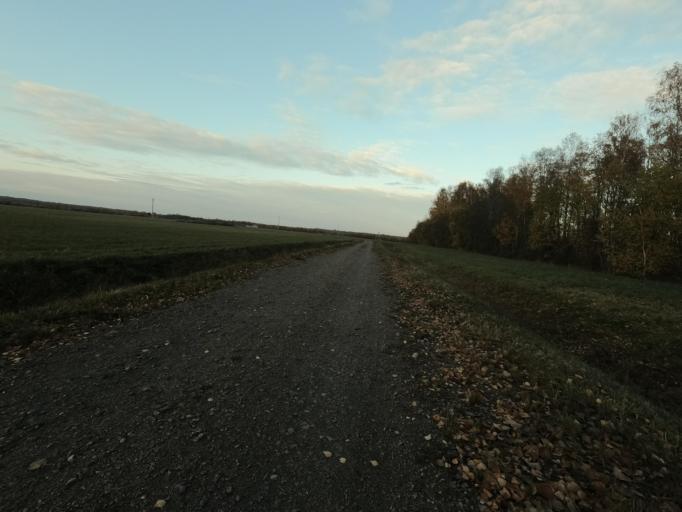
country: RU
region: Leningrad
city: Mga
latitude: 59.7845
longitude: 31.1968
